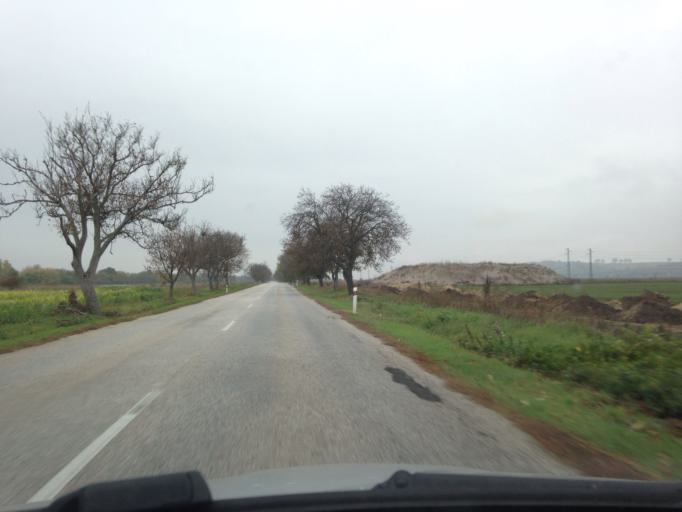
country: HU
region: Komarom-Esztergom
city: Tat
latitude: 47.8084
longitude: 18.6267
